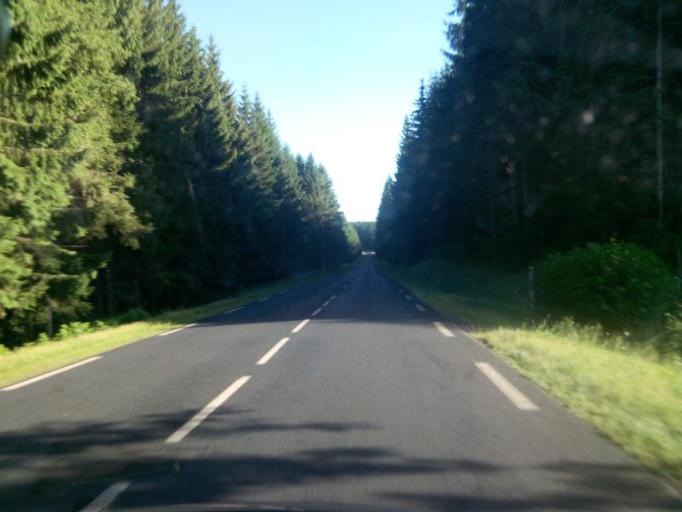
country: FR
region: Auvergne
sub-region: Departement de la Haute-Loire
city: Fontannes
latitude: 45.3024
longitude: 3.7018
